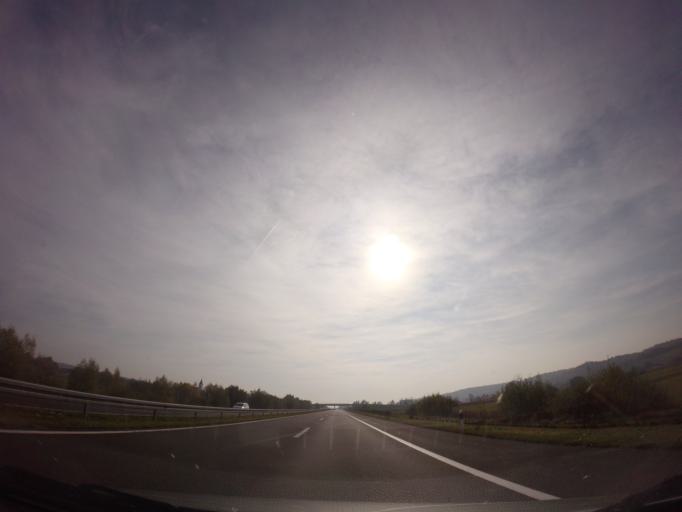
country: HR
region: Varazdinska
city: Remetinec
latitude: 46.0378
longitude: 16.2958
